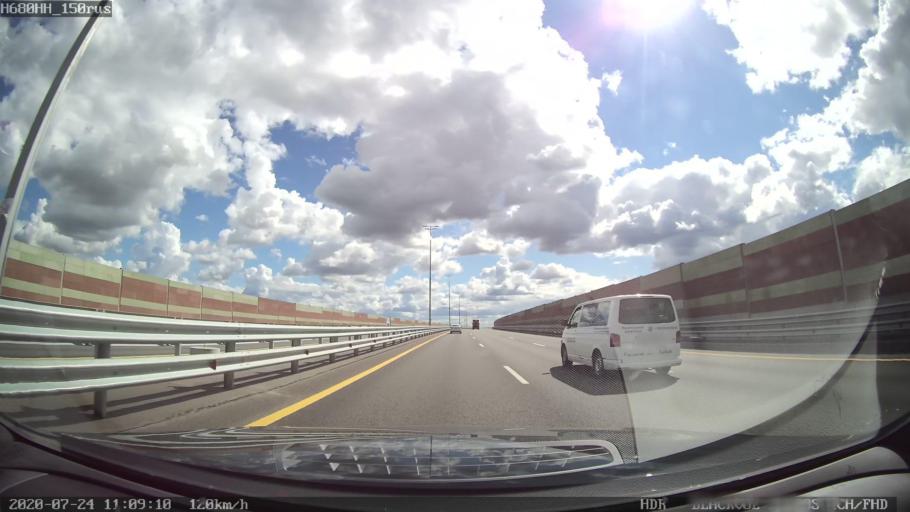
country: RU
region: St.-Petersburg
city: Tyarlevo
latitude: 59.7508
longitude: 30.4653
